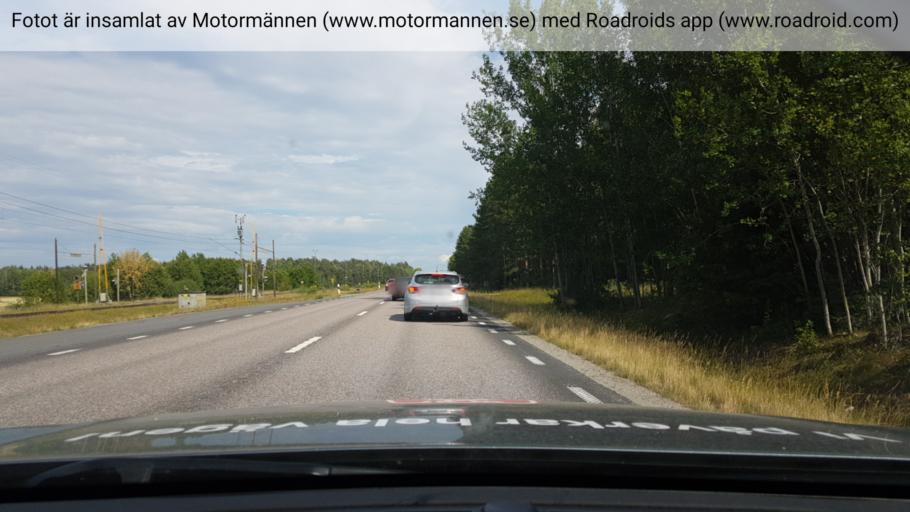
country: SE
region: Uppsala
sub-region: Enkopings Kommun
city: Orsundsbro
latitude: 59.8596
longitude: 17.3998
